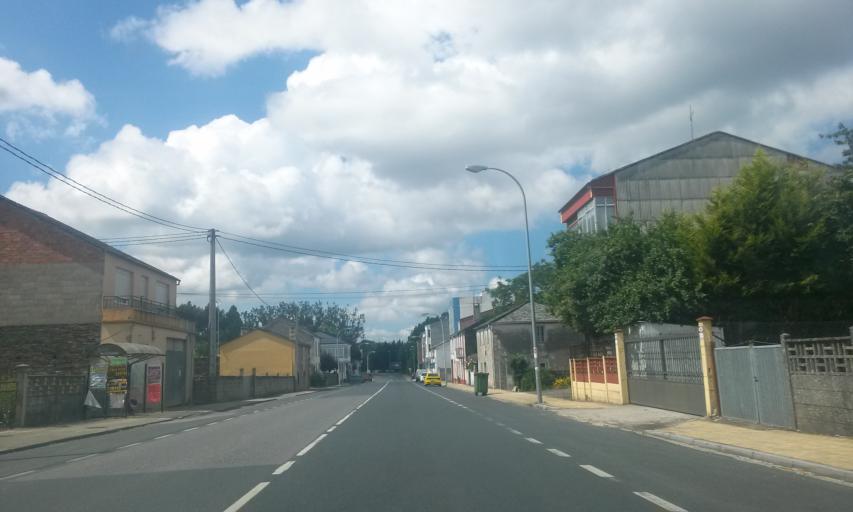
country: ES
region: Galicia
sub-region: Provincia de Lugo
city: Rabade
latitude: 43.1253
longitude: -7.6220
